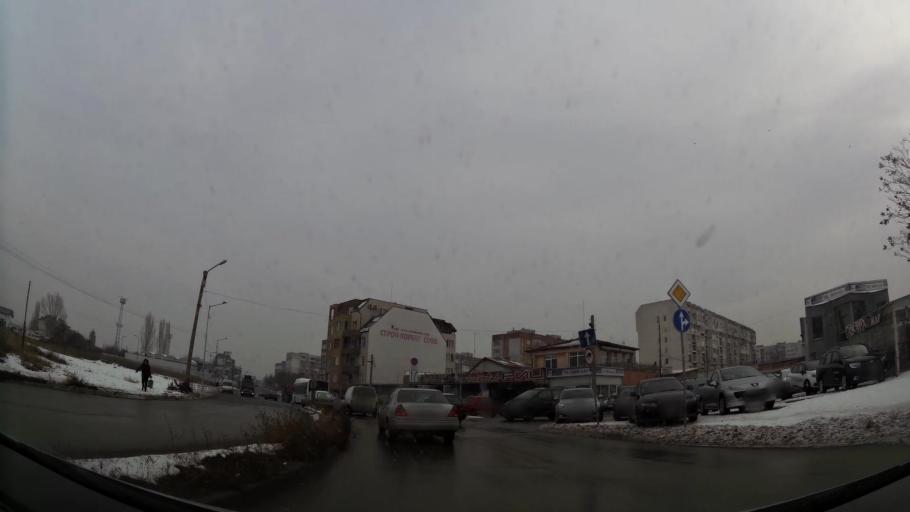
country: BG
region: Sofia-Capital
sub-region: Stolichna Obshtina
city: Sofia
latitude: 42.7070
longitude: 23.3407
